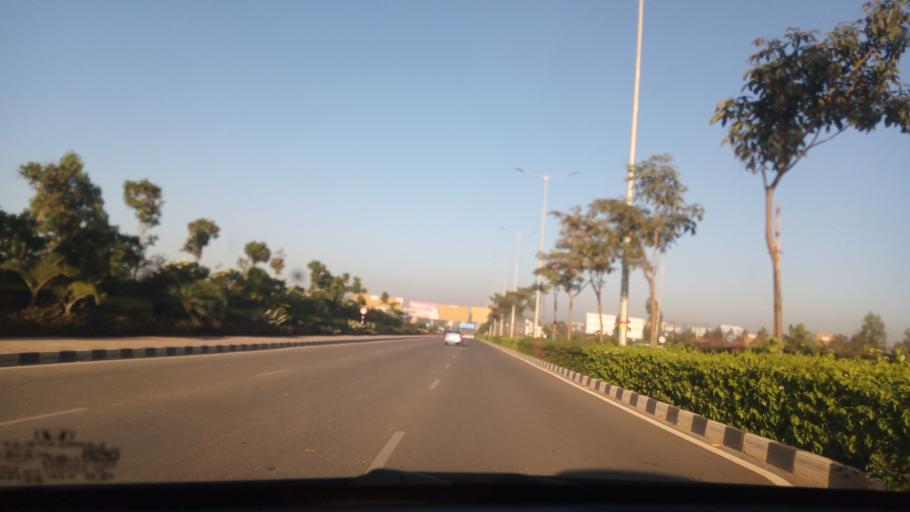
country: IN
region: Karnataka
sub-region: Bangalore Rural
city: Devanhalli
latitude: 13.1947
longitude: 77.6863
